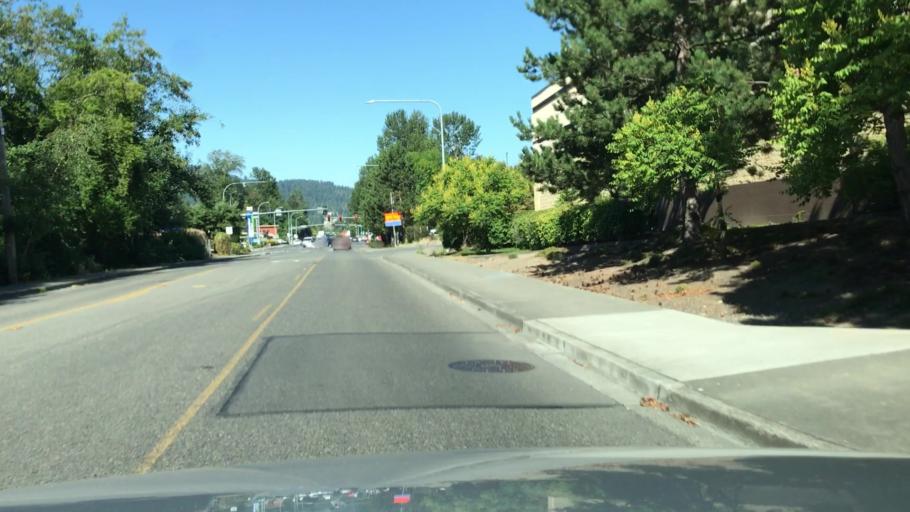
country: US
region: Washington
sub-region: King County
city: Issaquah
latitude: 47.5520
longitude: -122.0415
